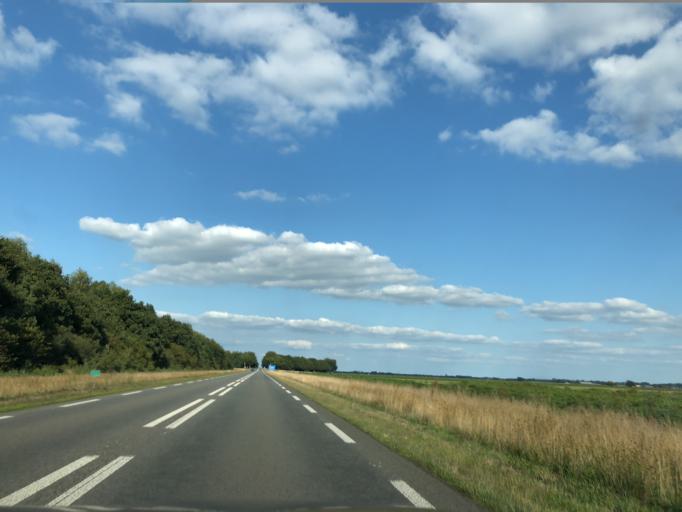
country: NL
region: Groningen
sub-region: Gemeente Stadskanaal
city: Stadskanaal
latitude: 52.9579
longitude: 6.8863
